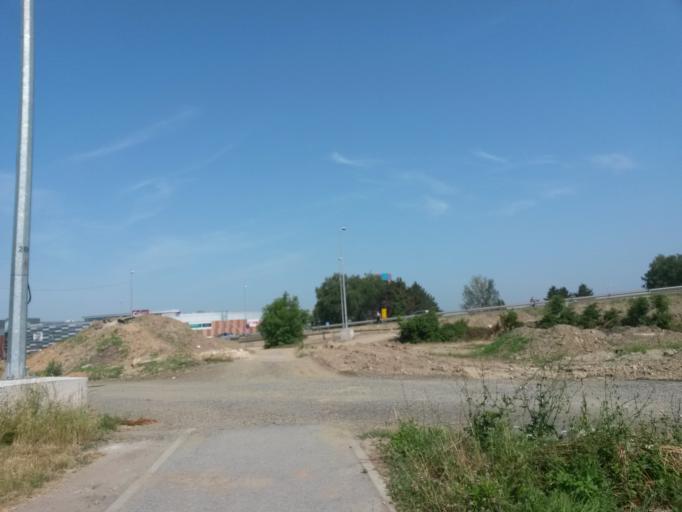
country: HR
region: Osjecko-Baranjska
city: Brijest
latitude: 45.5462
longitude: 18.6607
